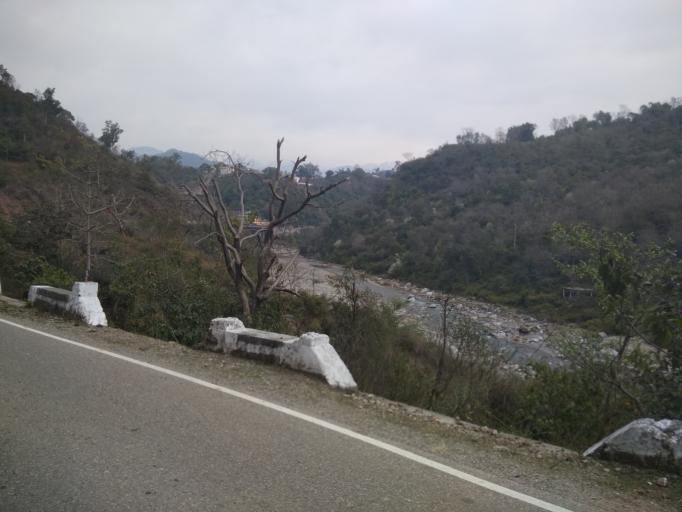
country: IN
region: Himachal Pradesh
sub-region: Kangra
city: Kotla
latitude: 32.2269
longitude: 76.0632
